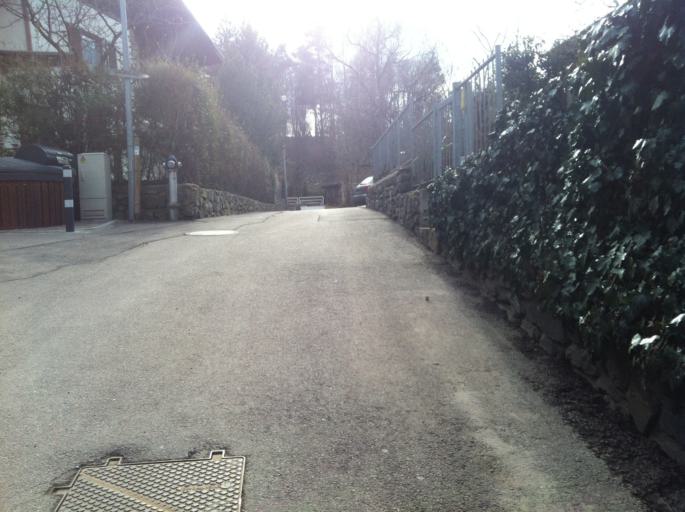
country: IT
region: Trentino-Alto Adige
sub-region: Bolzano
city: Bressanone
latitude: 46.7117
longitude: 11.6679
